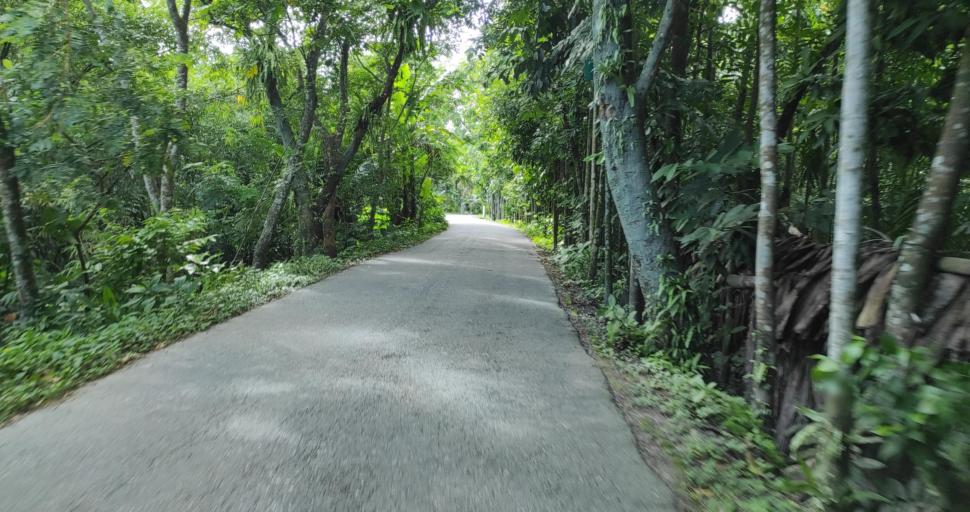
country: BD
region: Barisal
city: Gaurnadi
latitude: 22.8933
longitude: 90.1876
